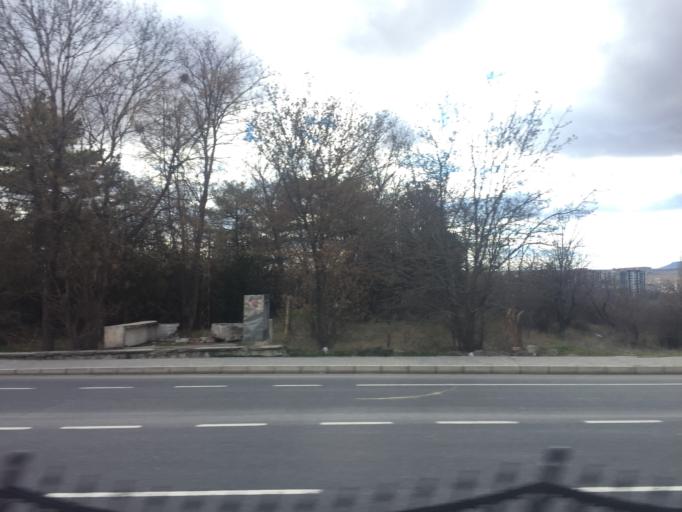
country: TR
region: Kirsehir
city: Kirsehir
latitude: 39.1615
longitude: 34.1587
